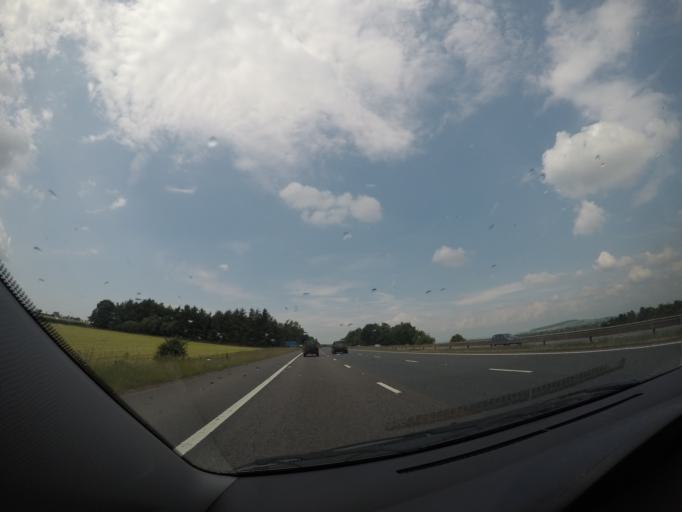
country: GB
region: England
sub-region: Cumbria
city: Scotby
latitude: 54.7683
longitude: -2.8416
